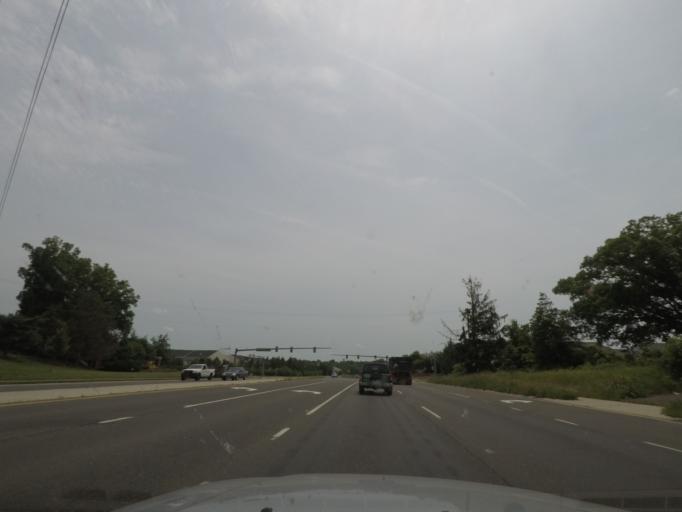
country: US
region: Virginia
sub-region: Prince William County
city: Haymarket
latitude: 38.8279
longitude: -77.6335
